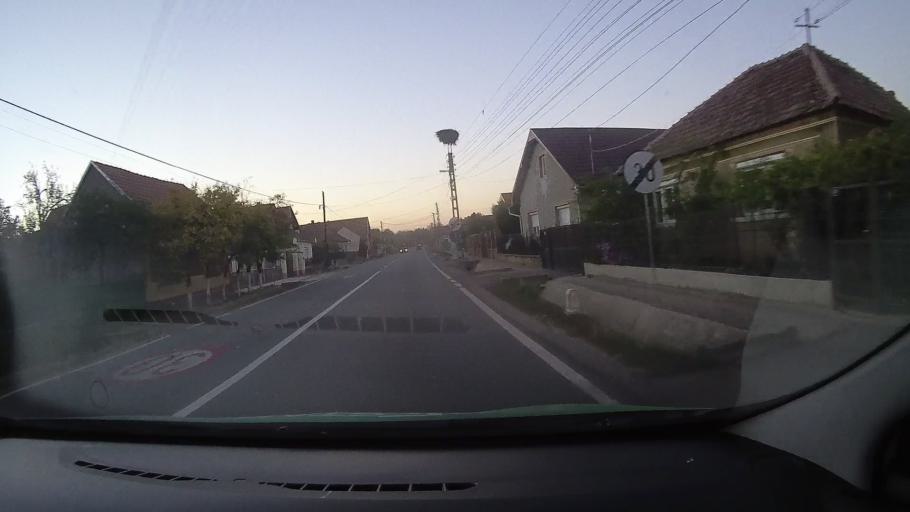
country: RO
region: Bihor
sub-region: Comuna Tarcea
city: Tarcea
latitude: 47.4584
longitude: 22.1716
